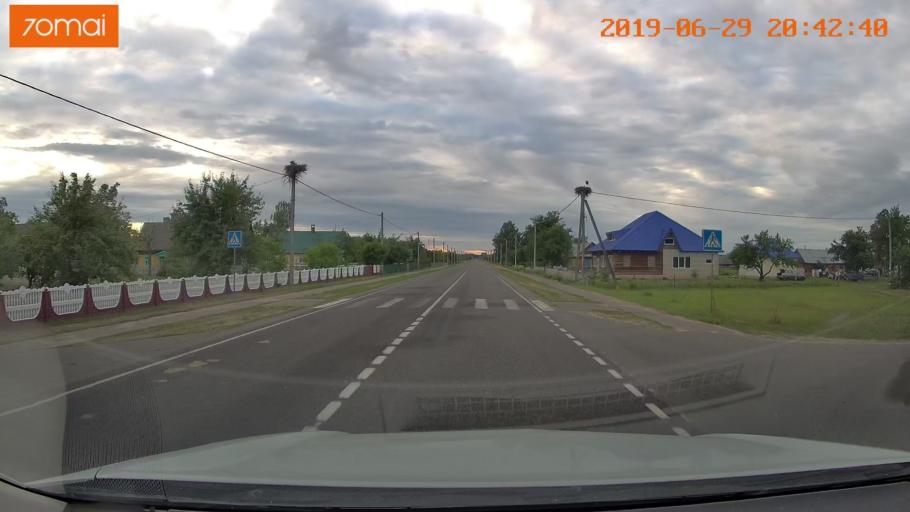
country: BY
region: Brest
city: Hantsavichy
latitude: 52.5995
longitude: 26.3234
